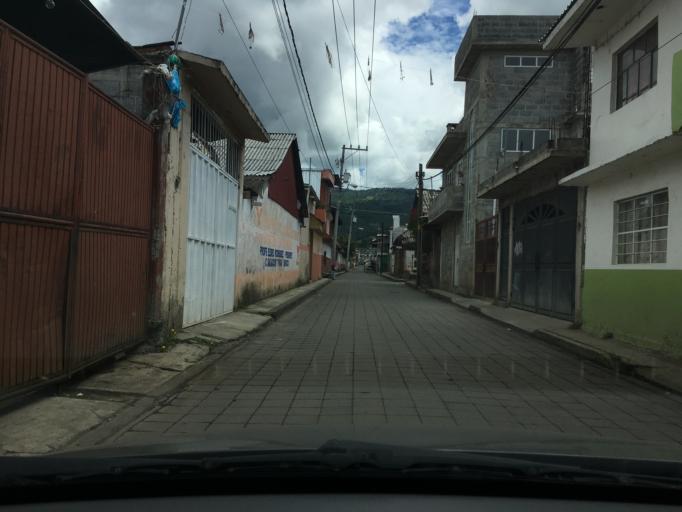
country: MX
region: Michoacan
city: Nahuatzen
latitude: 19.6536
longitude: -101.9190
